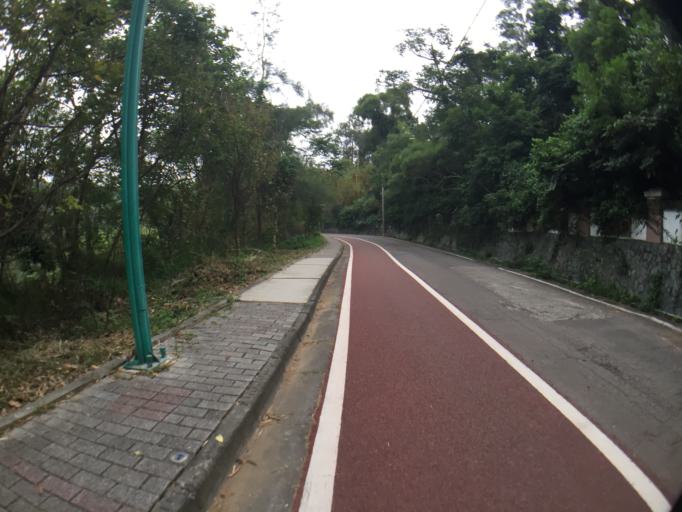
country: TW
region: Taiwan
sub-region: Hsinchu
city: Hsinchu
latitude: 24.7728
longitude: 120.9737
